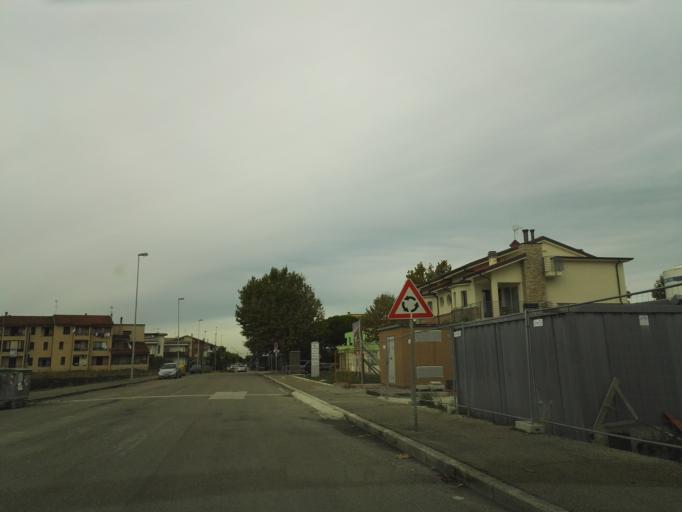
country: IT
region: The Marches
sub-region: Provincia di Pesaro e Urbino
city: Marotta
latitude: 43.7643
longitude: 13.1402
